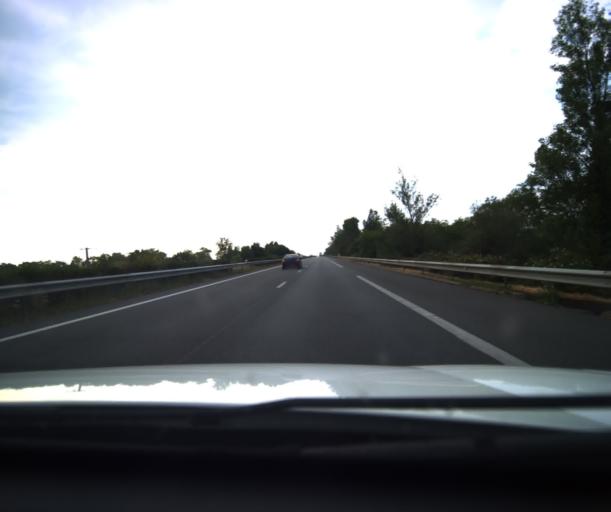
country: FR
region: Midi-Pyrenees
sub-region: Departement du Tarn-et-Garonne
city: Saint-Porquier
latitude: 44.0311
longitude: 1.1618
